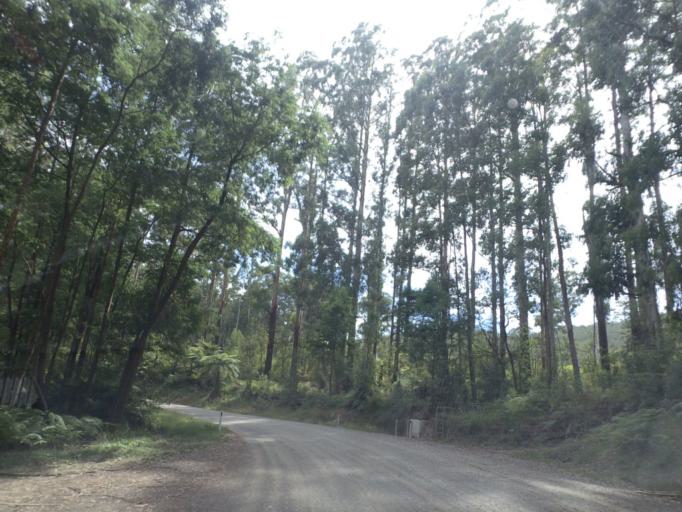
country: AU
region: Victoria
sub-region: Yarra Ranges
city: Healesville
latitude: -37.5548
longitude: 145.5134
